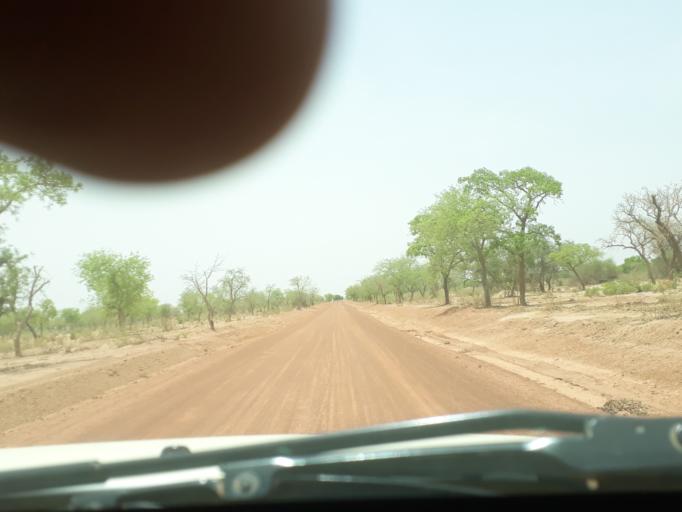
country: BF
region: Plateau-Central
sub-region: Province d'Oubritenga
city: Ziniare
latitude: 12.5802
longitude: -1.3371
